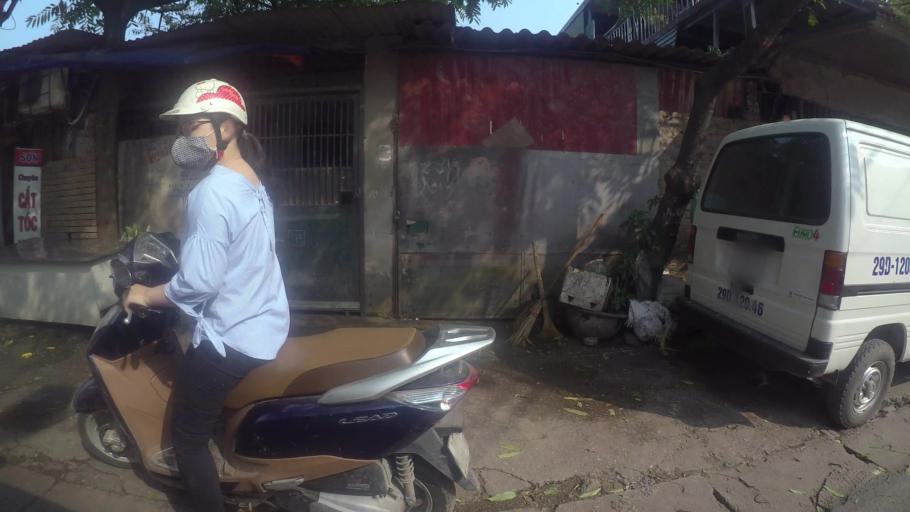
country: VN
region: Ha Noi
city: Tay Ho
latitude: 21.0587
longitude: 105.8079
